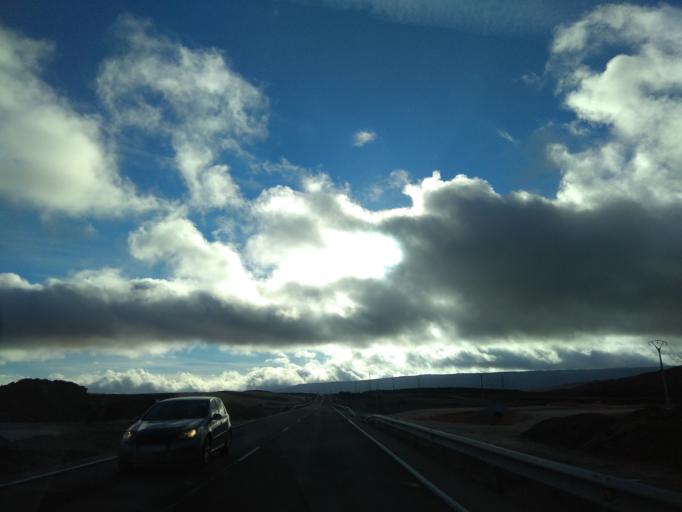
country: ES
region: Castille and Leon
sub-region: Provincia de Palencia
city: Pomar de Valdivia
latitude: 42.7588
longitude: -4.1821
